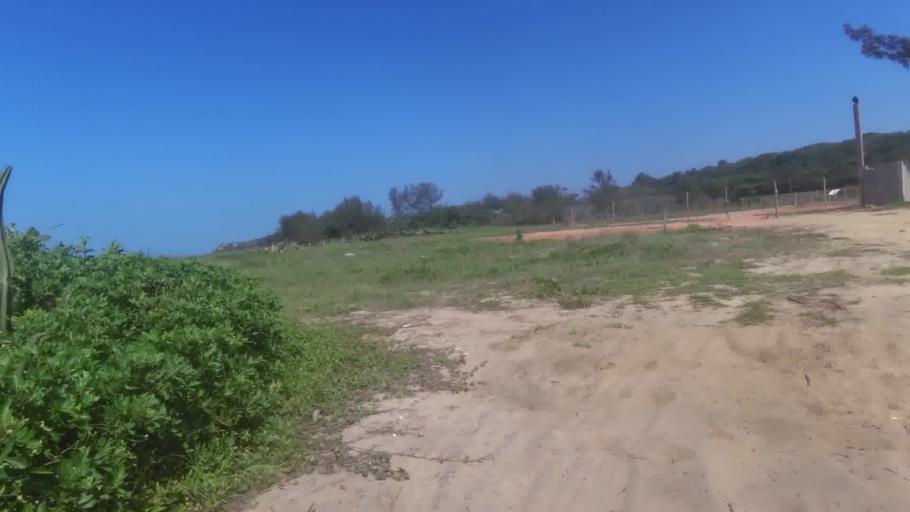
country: BR
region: Espirito Santo
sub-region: Marataizes
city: Marataizes
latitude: -21.1146
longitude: -40.8551
